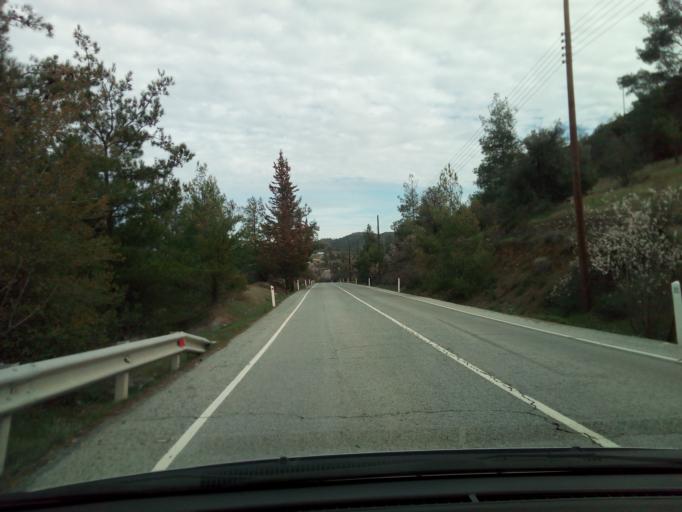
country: CY
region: Lefkosia
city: Klirou
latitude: 34.9764
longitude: 33.1529
